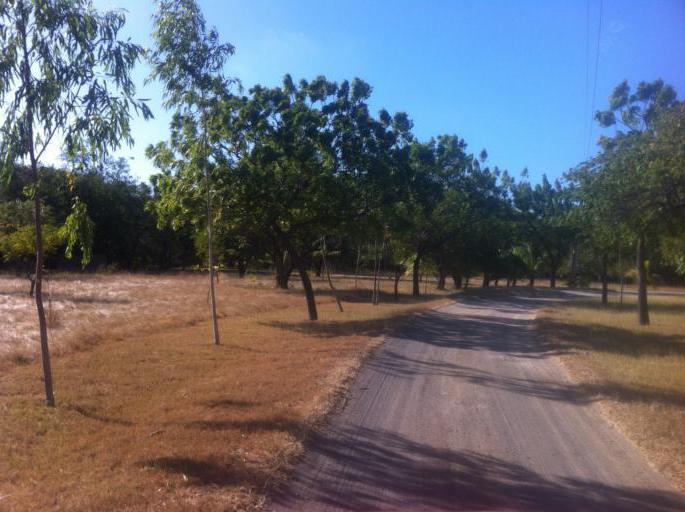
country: NI
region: Managua
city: Carlos Fonseca Amador
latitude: 11.9023
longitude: -86.6092
